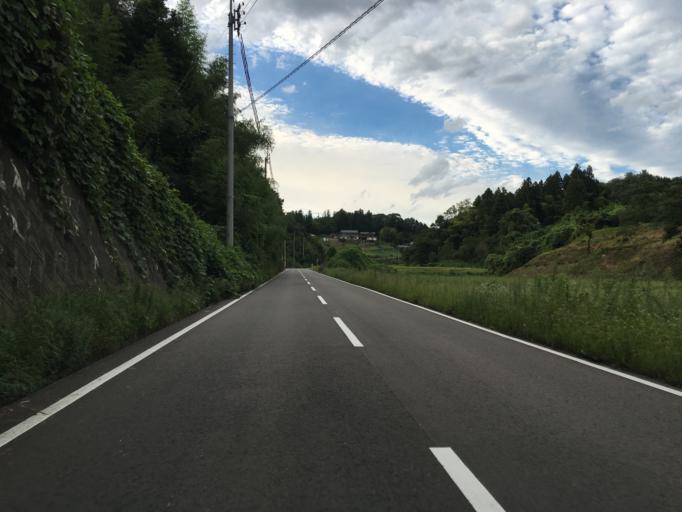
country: JP
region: Fukushima
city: Nihommatsu
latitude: 37.6015
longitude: 140.4984
